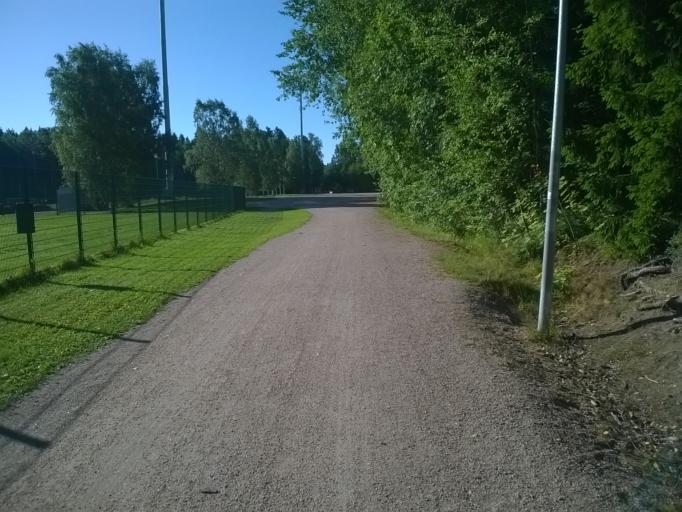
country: FI
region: Uusimaa
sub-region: Helsinki
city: Helsinki
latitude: 60.2351
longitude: 24.9120
